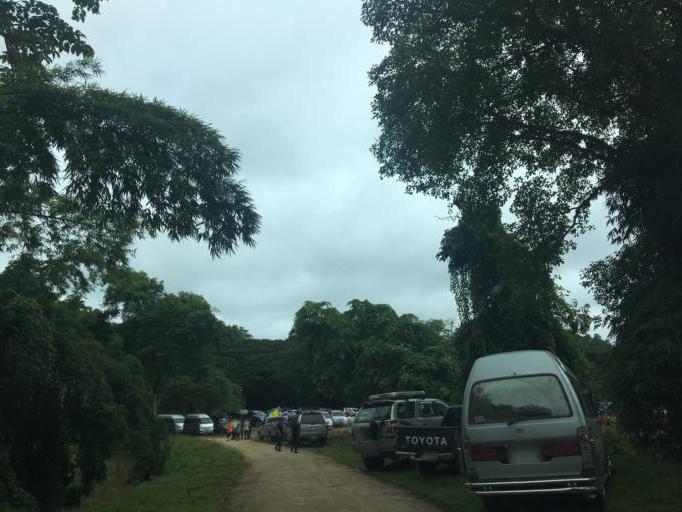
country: TH
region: Chiang Rai
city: Mae Lao
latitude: 19.6936
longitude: 99.6561
